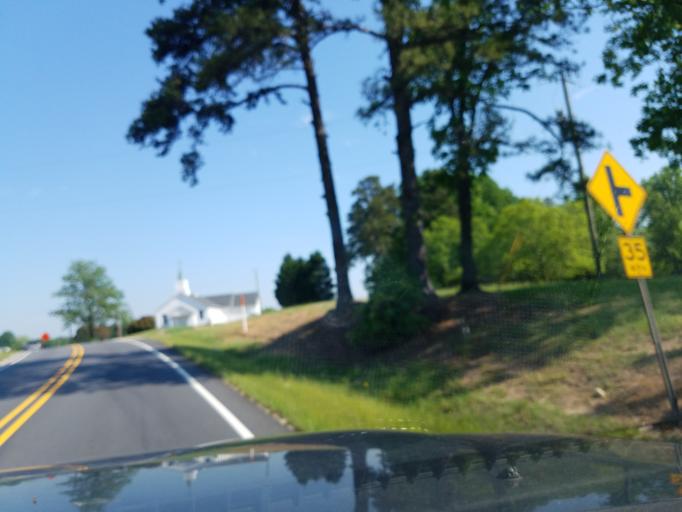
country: US
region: North Carolina
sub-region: Vance County
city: Henderson
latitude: 36.3528
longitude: -78.4519
